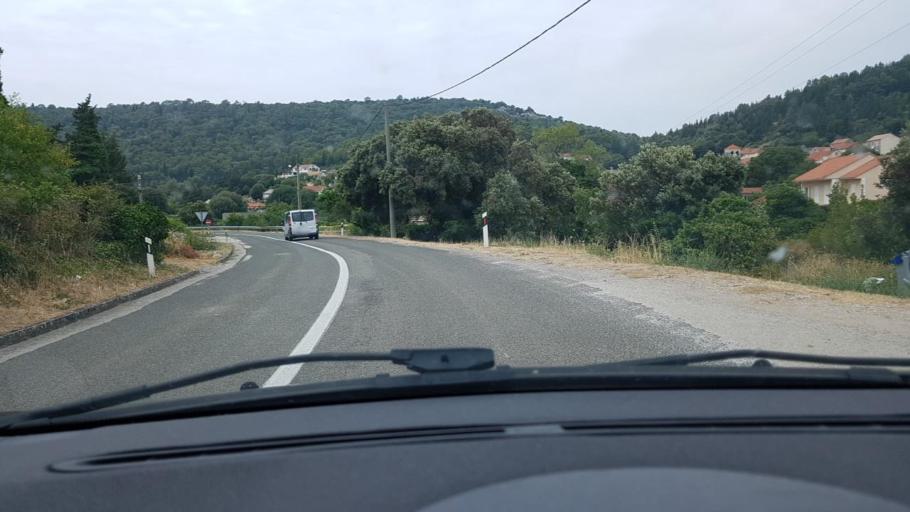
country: HR
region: Dubrovacko-Neretvanska
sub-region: Grad Korcula
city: Zrnovo
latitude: 42.9495
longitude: 17.0389
